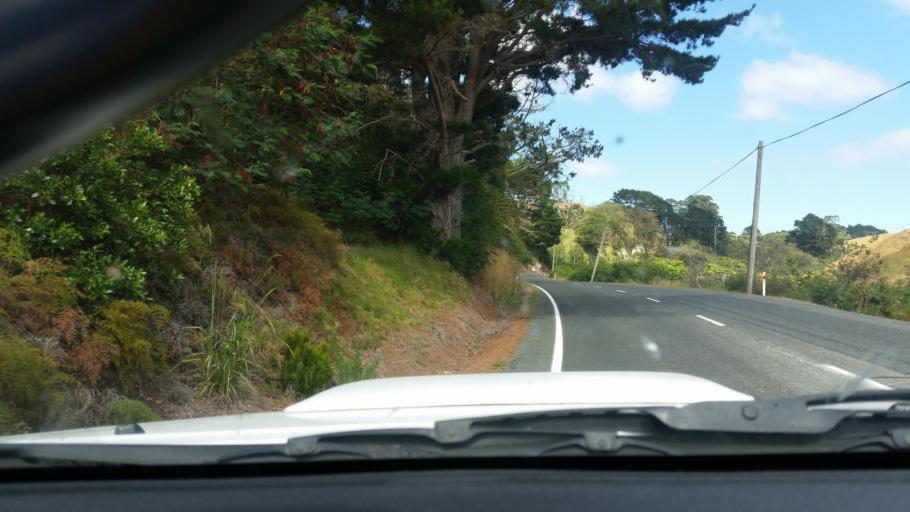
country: NZ
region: Northland
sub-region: Kaipara District
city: Dargaville
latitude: -35.8225
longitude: 173.6972
